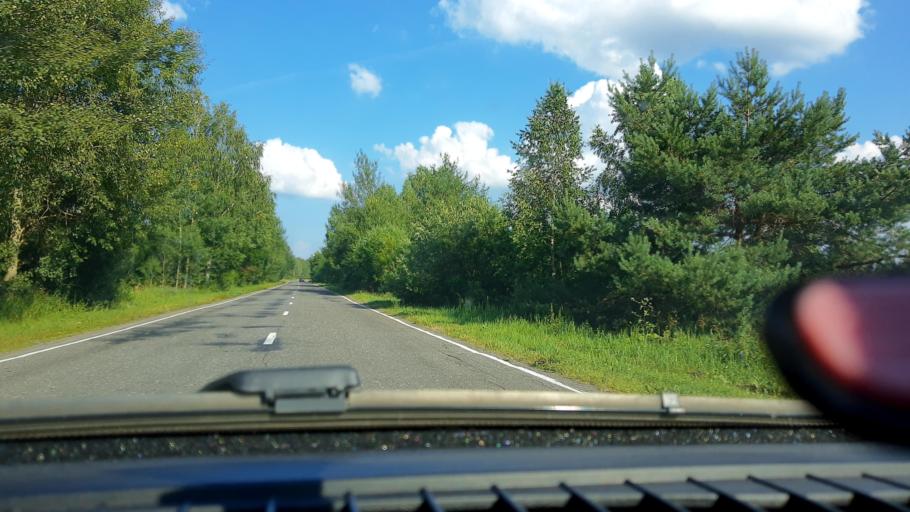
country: RU
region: Nizjnij Novgorod
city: Neklyudovo
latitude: 56.5112
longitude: 43.9523
